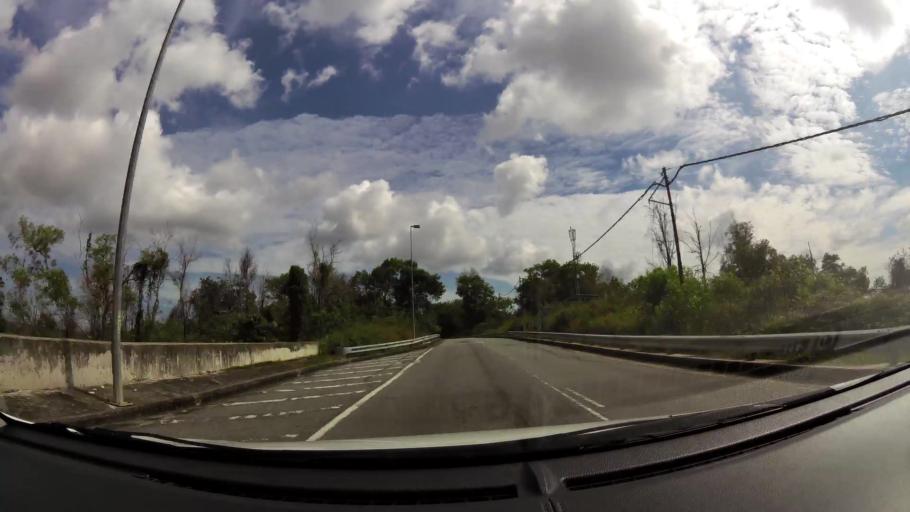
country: BN
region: Brunei and Muara
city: Bandar Seri Begawan
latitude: 4.9315
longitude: 114.9048
